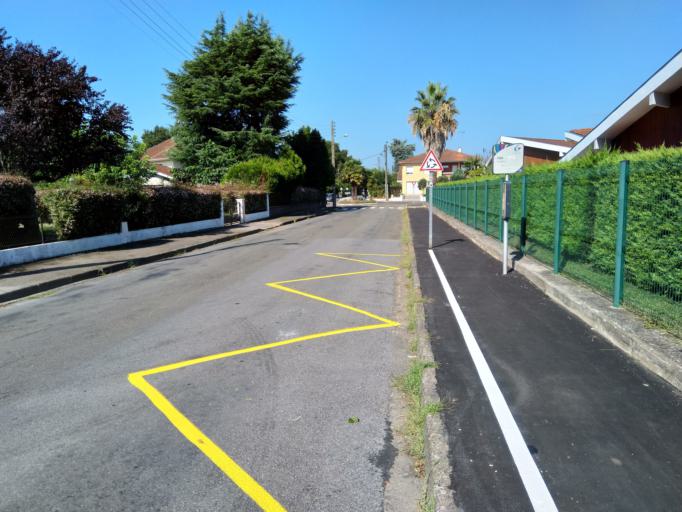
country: FR
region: Aquitaine
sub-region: Departement des Landes
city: Saint-Paul-les-Dax
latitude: 43.7292
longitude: -1.0508
